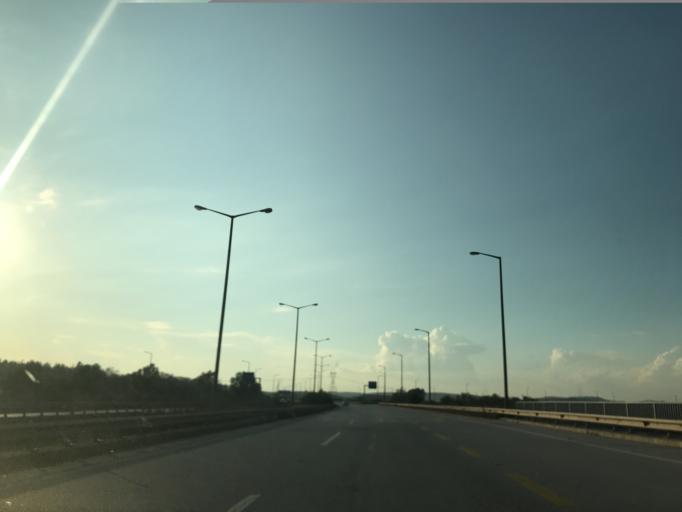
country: TR
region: Osmaniye
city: Toprakkale
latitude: 36.9746
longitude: 36.0206
